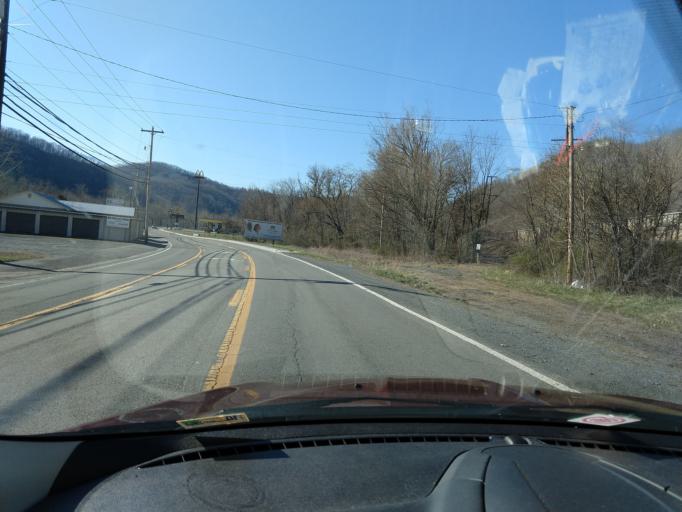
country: US
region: West Virginia
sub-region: Summers County
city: Hinton
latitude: 37.6550
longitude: -80.8848
